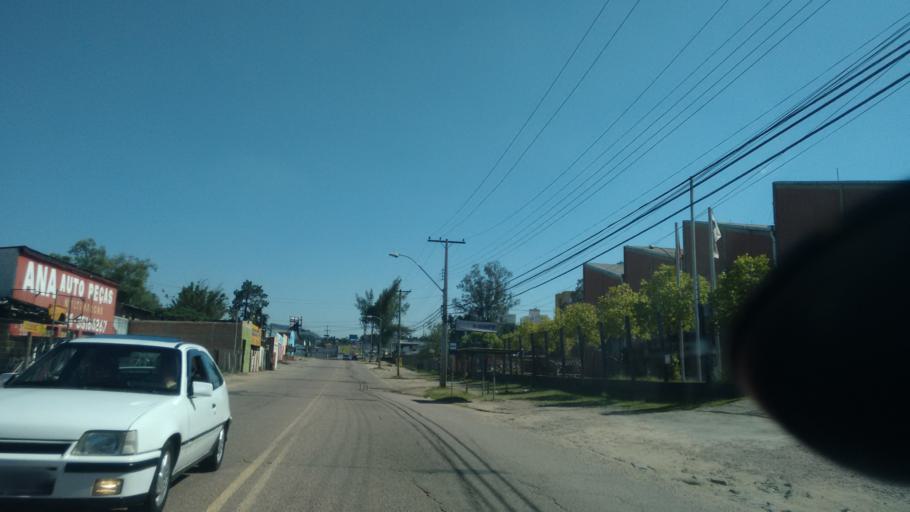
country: BR
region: Rio Grande do Sul
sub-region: Cachoeirinha
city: Cachoeirinha
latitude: -30.0094
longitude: -51.1282
